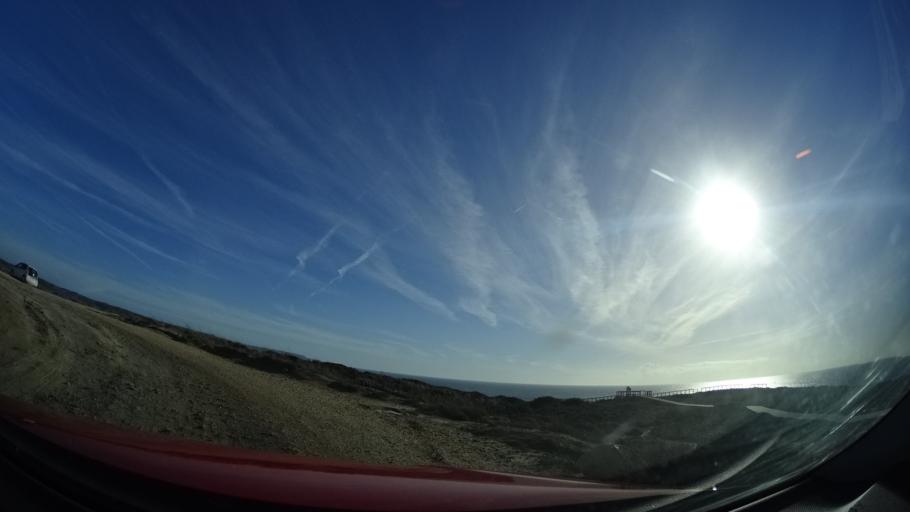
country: PT
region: Faro
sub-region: Vila do Bispo
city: Vila do Bispo
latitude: 37.1959
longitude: -8.9166
